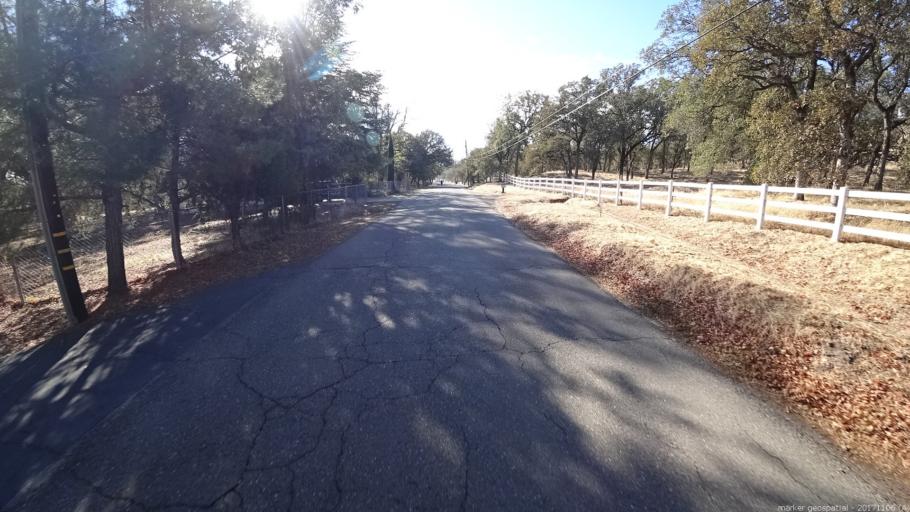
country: US
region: California
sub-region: Shasta County
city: Palo Cedro
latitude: 40.5353
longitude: -122.2476
